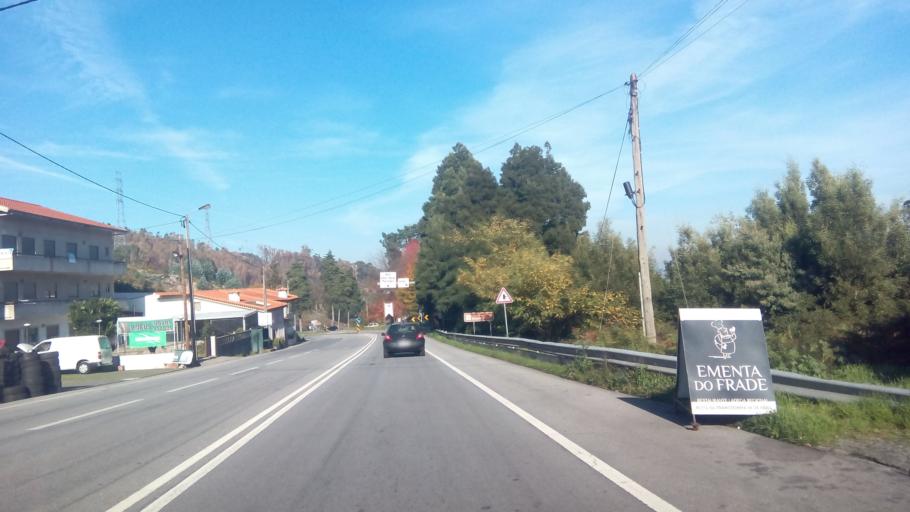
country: PT
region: Porto
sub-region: Paredes
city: Baltar
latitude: 41.1921
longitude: -8.3660
